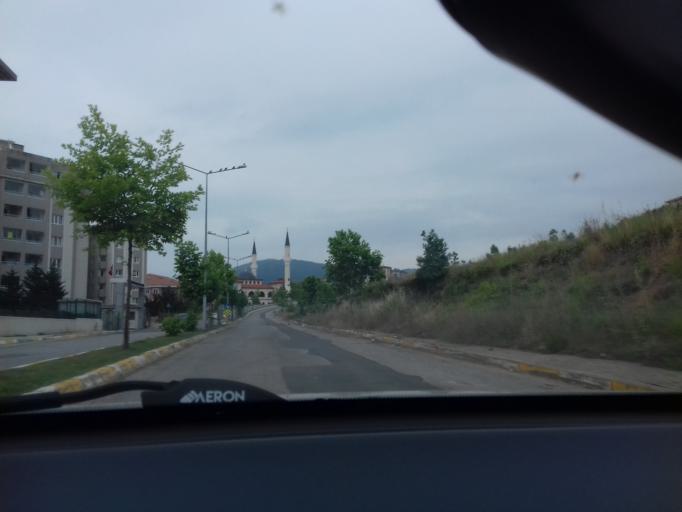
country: TR
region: Istanbul
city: Sultanbeyli
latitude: 40.9331
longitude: 29.3006
